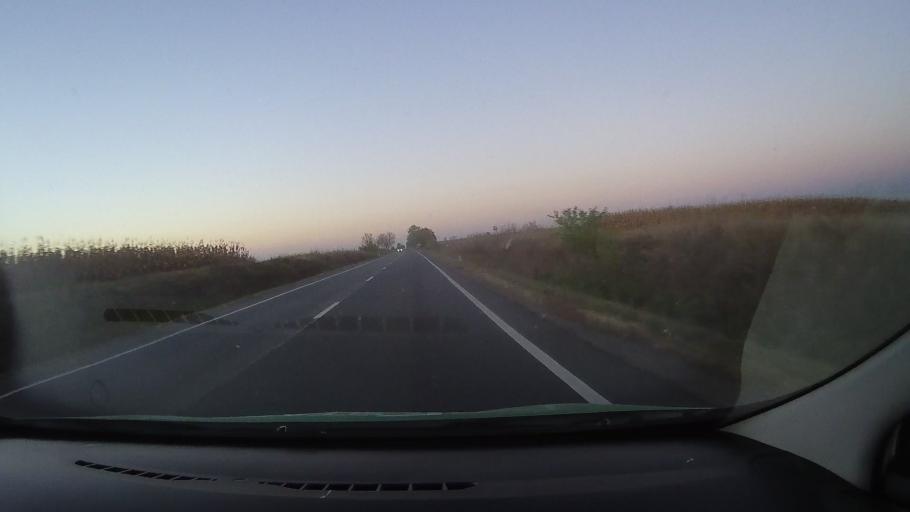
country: RO
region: Bihor
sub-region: Comuna Tarcea
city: Tarcea
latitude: 47.4696
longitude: 22.1655
